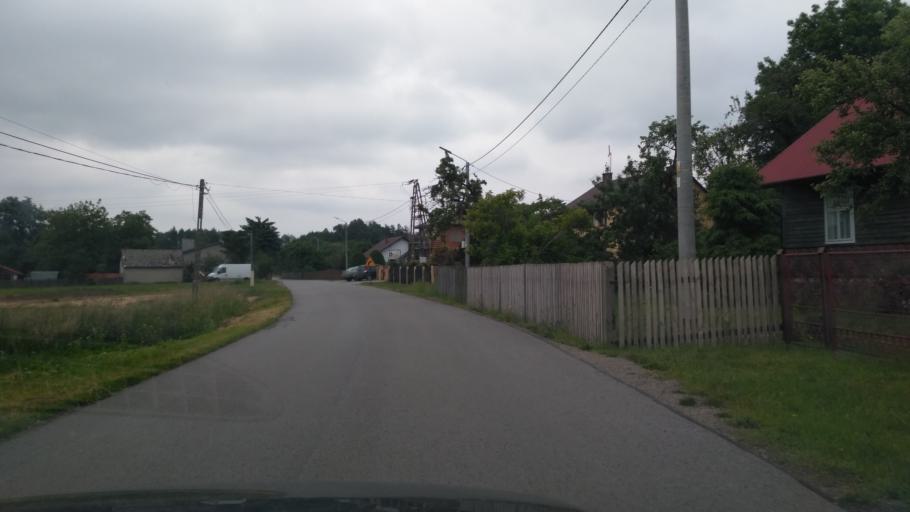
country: PL
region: Subcarpathian Voivodeship
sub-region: Powiat kolbuszowski
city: Niwiska
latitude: 50.2175
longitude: 21.6381
